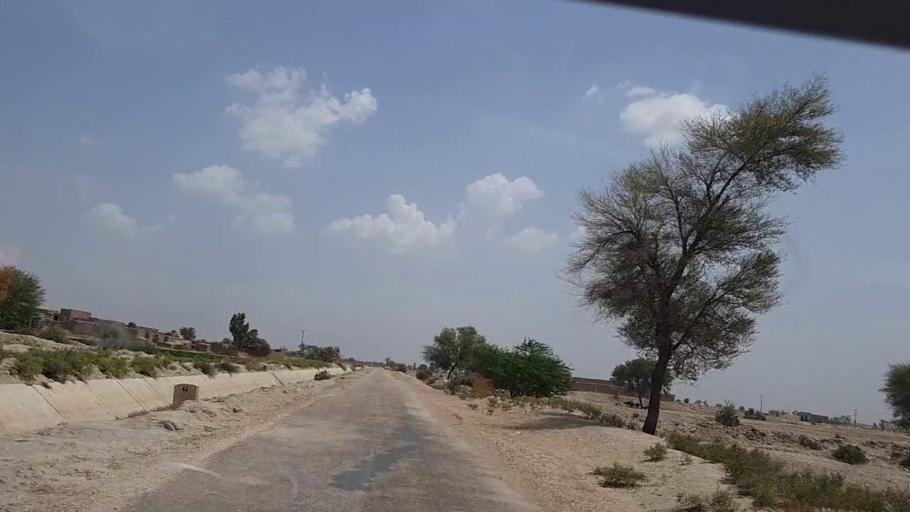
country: PK
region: Sindh
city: Bhan
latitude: 26.5304
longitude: 67.6330
